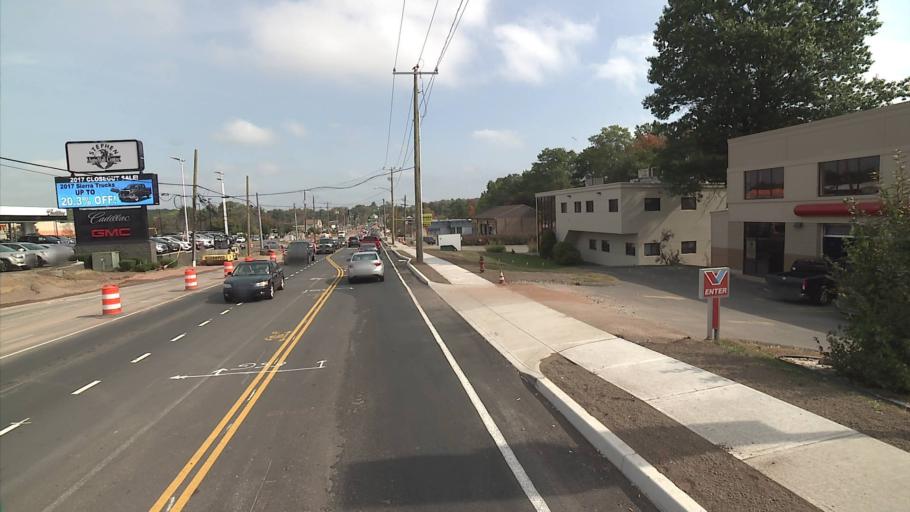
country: US
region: Connecticut
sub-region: Hartford County
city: Bristol
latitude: 41.6960
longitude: -72.9076
